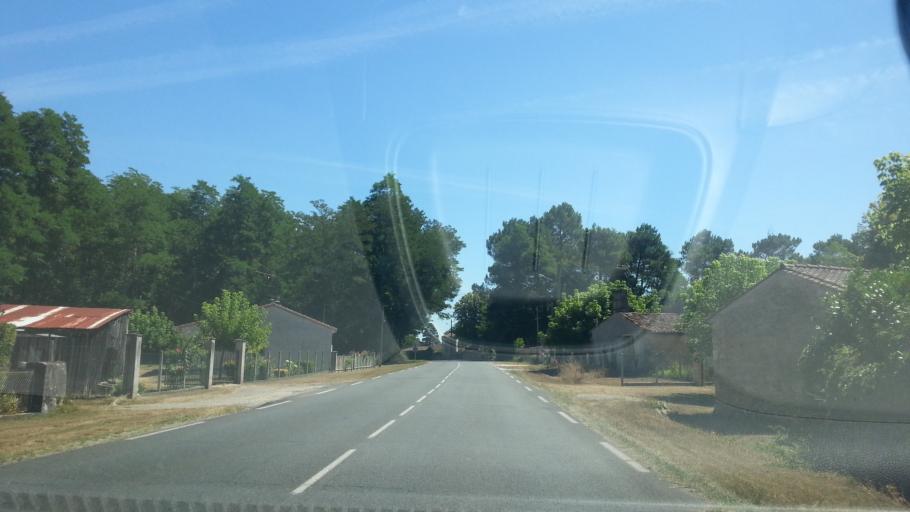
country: FR
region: Aquitaine
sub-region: Departement de la Gironde
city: Landiras
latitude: 44.5615
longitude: -0.3904
